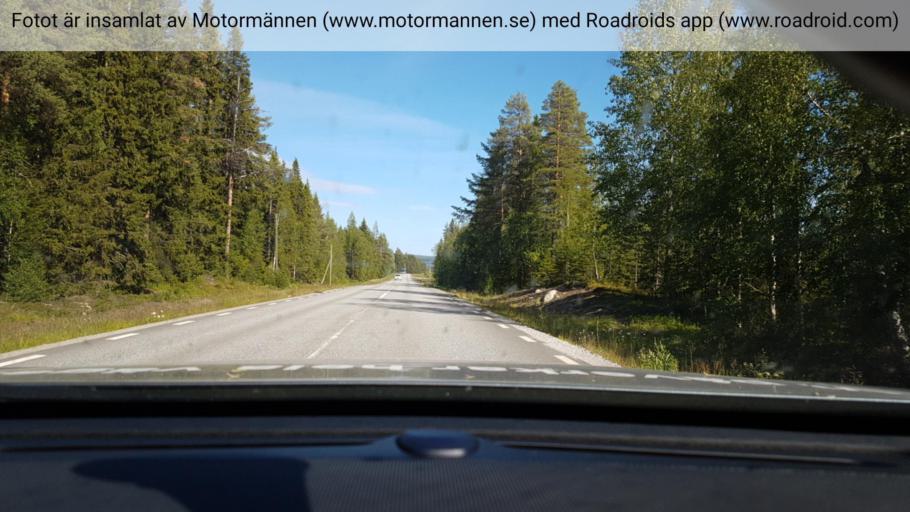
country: SE
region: Vaesterbotten
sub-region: Lycksele Kommun
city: Lycksele
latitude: 64.6490
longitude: 18.4713
